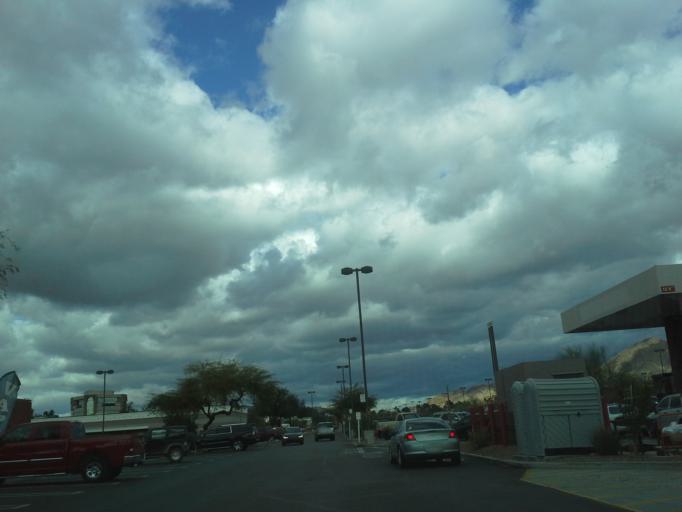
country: US
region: Arizona
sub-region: Maricopa County
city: Paradise Valley
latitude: 33.4733
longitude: -111.9858
